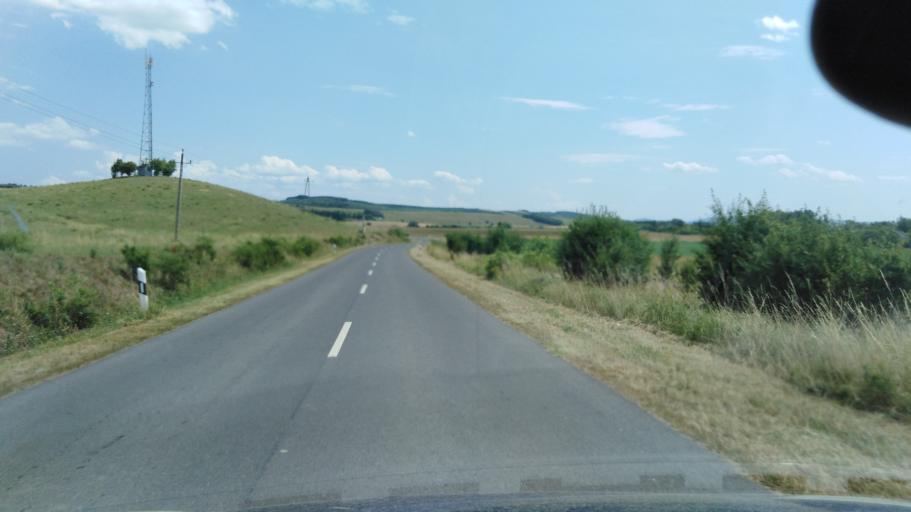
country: HU
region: Nograd
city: Szecseny
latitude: 48.1754
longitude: 19.5264
